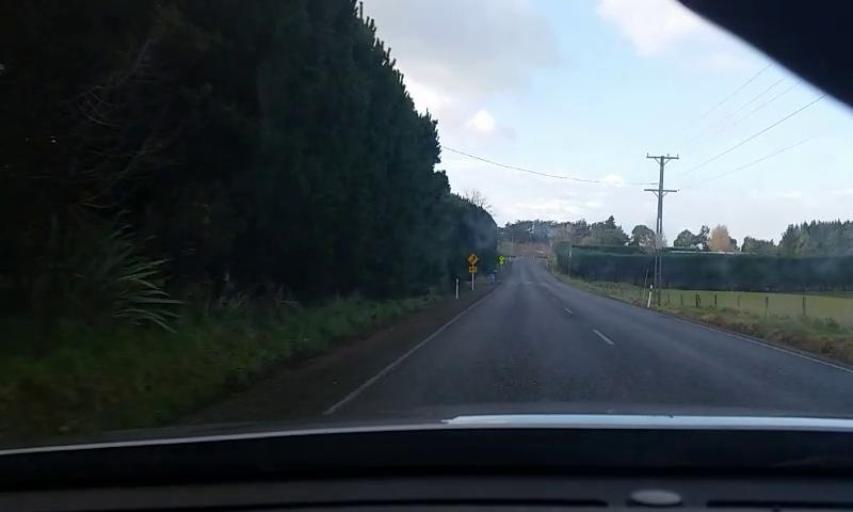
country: NZ
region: Southland
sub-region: Invercargill City
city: Invercargill
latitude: -46.3806
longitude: 168.4341
